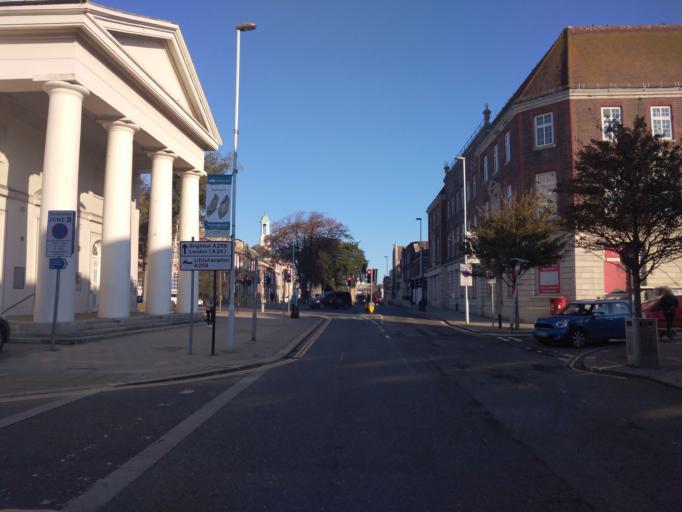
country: GB
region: England
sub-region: West Sussex
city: Worthing
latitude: 50.8135
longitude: -0.3709
